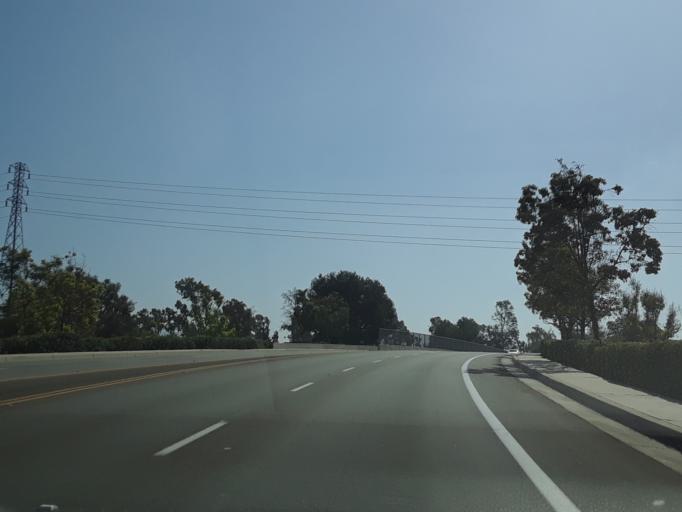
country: US
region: California
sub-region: Orange County
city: Irvine
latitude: 33.6739
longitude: -117.8314
